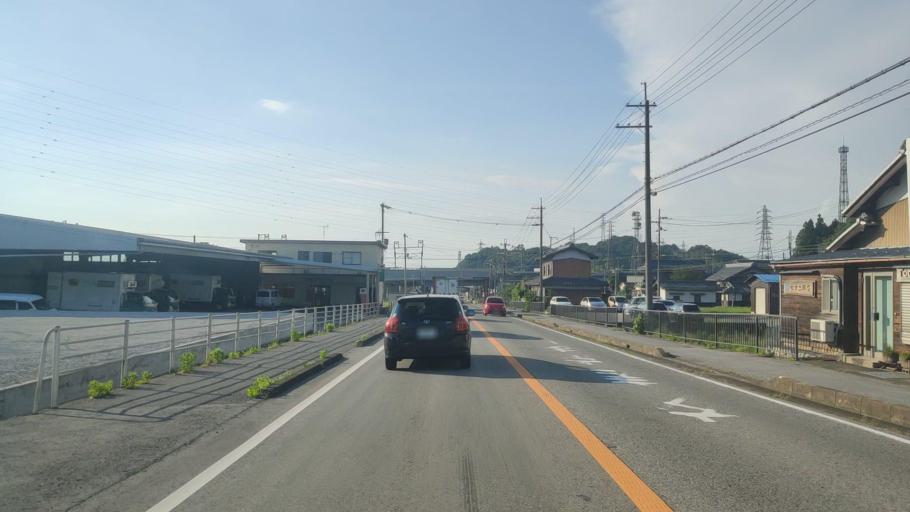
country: JP
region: Shiga Prefecture
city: Hikone
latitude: 35.2543
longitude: 136.2764
